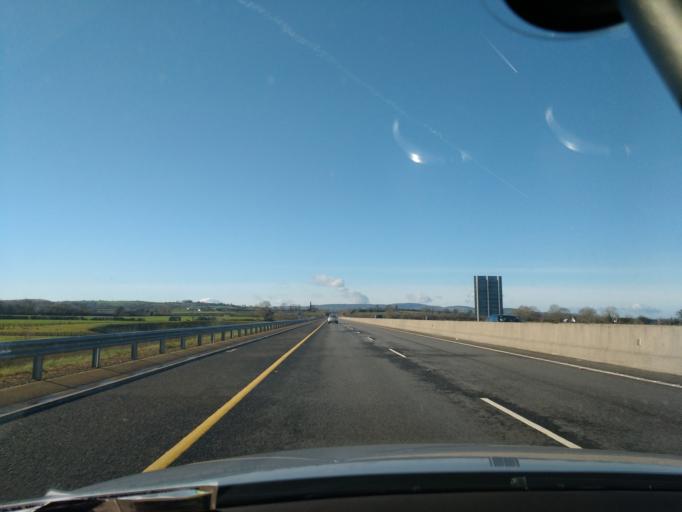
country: IE
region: Munster
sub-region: North Tipperary
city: Nenagh
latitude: 52.8471
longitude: -8.1844
